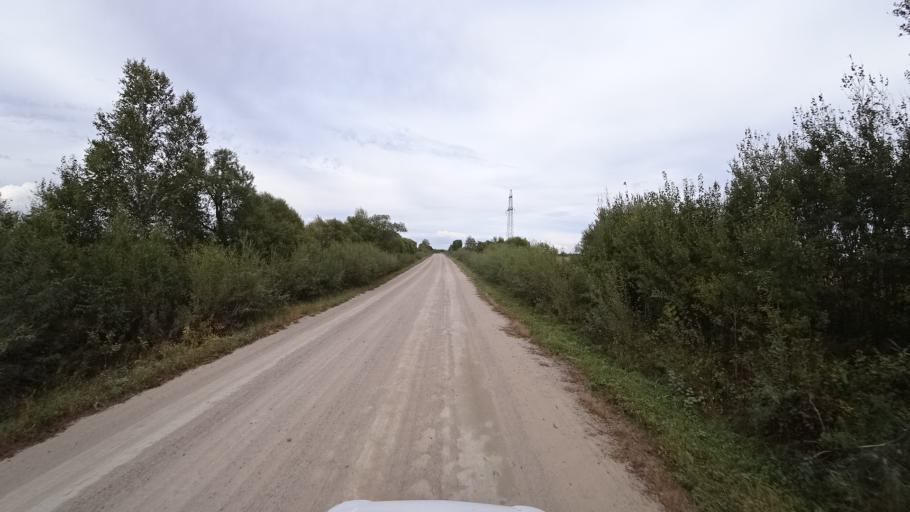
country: RU
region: Amur
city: Arkhara
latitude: 49.3728
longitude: 130.1468
